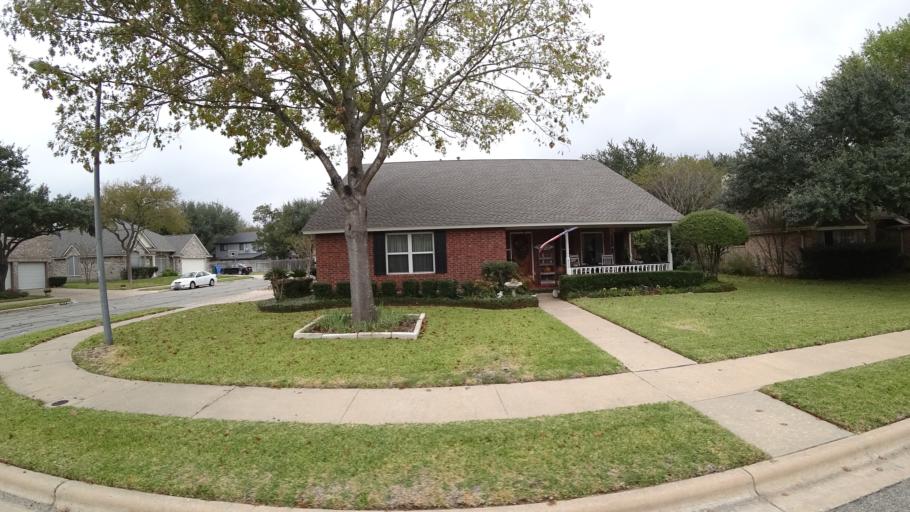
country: US
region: Texas
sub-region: Travis County
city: Pflugerville
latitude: 30.4457
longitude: -97.6115
